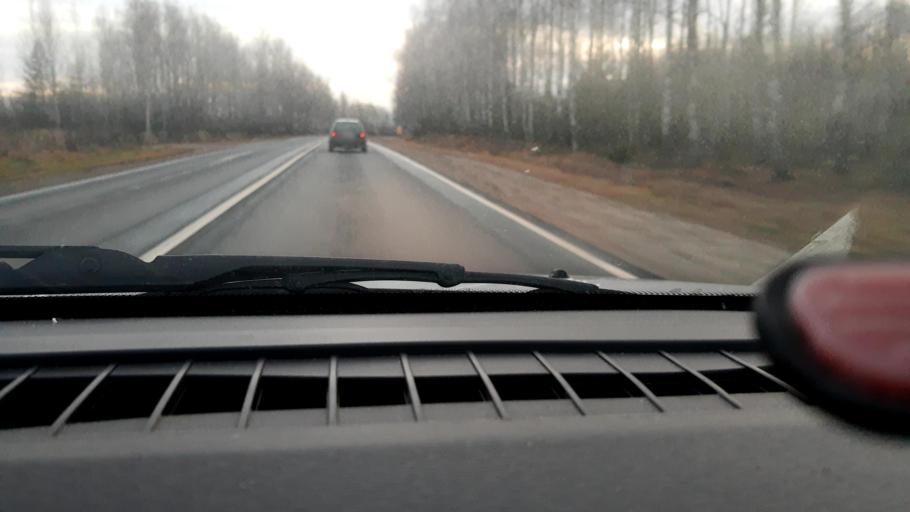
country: RU
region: Nizjnij Novgorod
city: Krasnyye Baki
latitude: 57.0780
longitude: 45.1442
